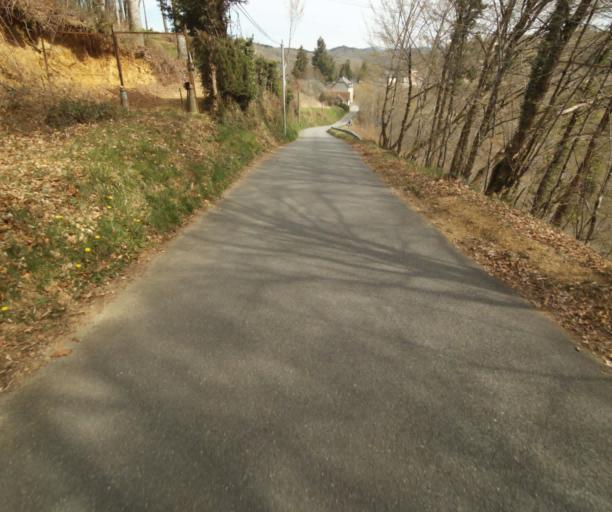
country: FR
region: Limousin
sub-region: Departement de la Correze
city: Naves
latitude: 45.3429
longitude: 1.8115
